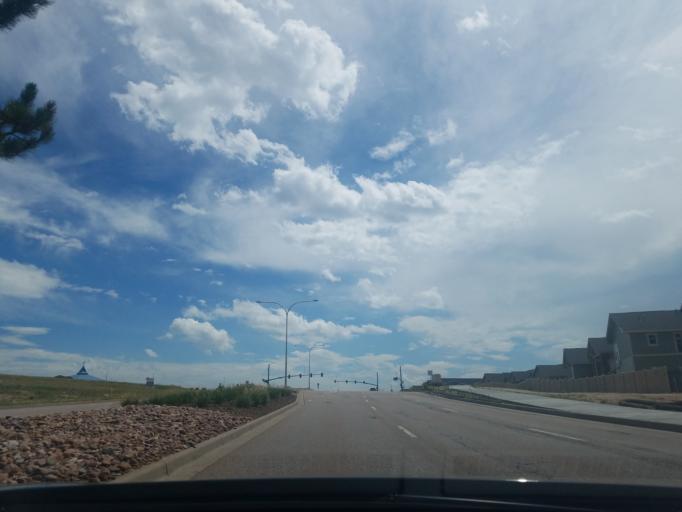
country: US
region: Colorado
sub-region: El Paso County
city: Gleneagle
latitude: 38.9964
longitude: -104.7981
